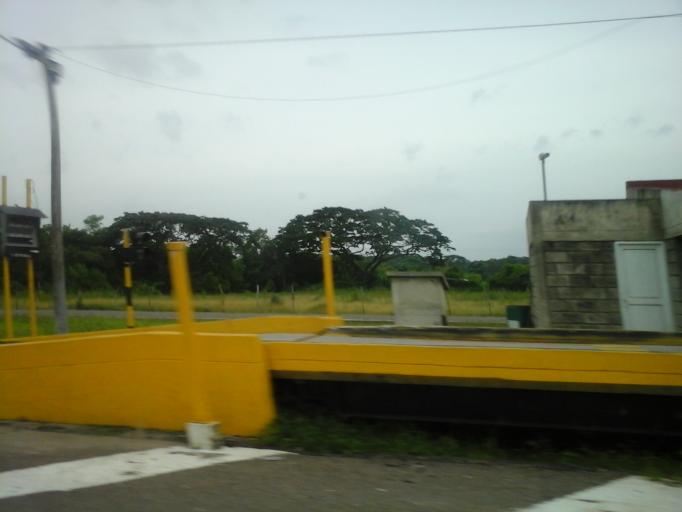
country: CO
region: Bolivar
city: San Pablo
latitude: 10.1364
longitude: -75.2673
